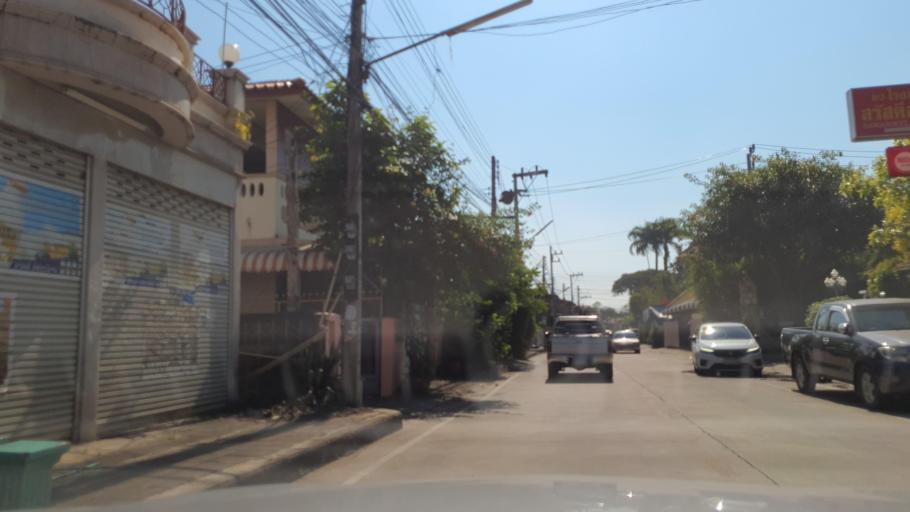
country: TH
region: Nan
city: Nan
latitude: 18.7745
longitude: 100.7682
